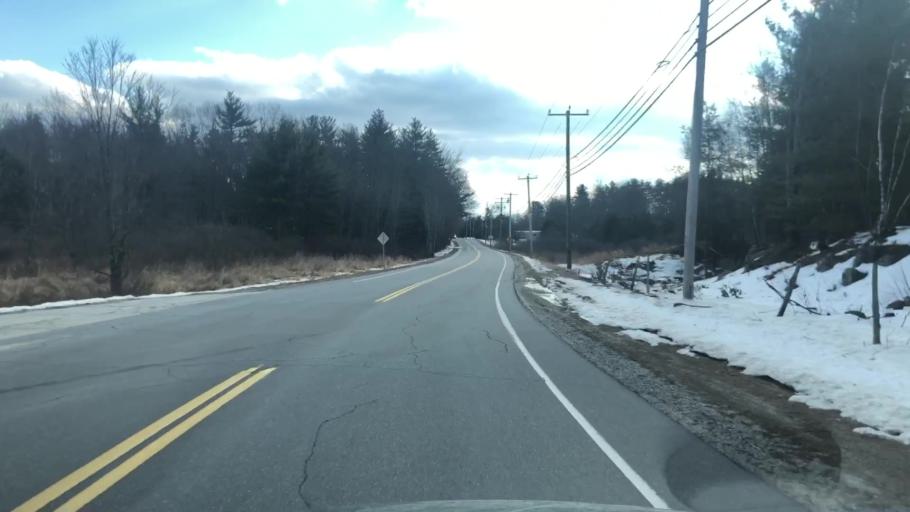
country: US
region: New Hampshire
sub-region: Hillsborough County
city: Milford
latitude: 42.8535
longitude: -71.6633
